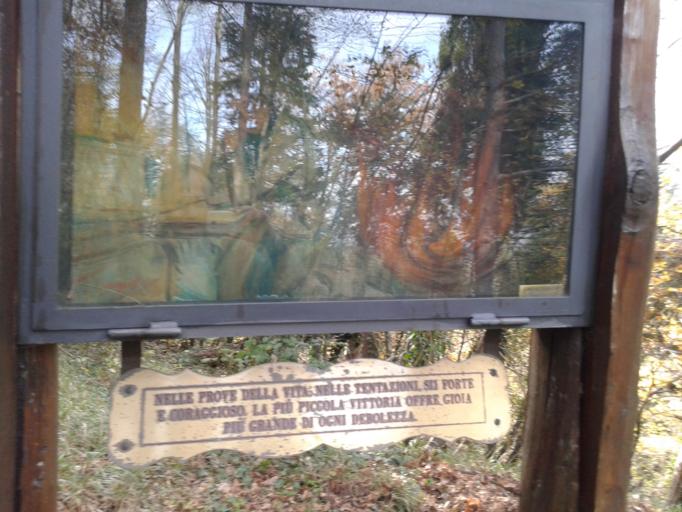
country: IT
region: Emilia-Romagna
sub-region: Forli-Cesena
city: Dovadola
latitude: 44.1545
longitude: 11.8792
